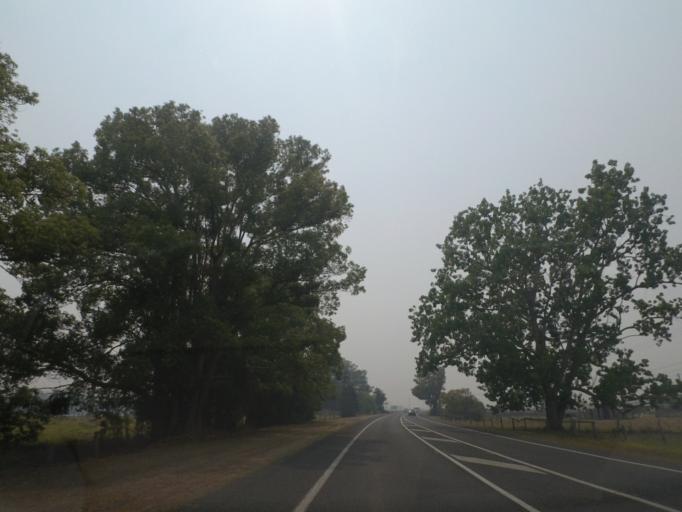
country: AU
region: New South Wales
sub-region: Clarence Valley
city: Maclean
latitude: -29.5647
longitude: 153.1047
